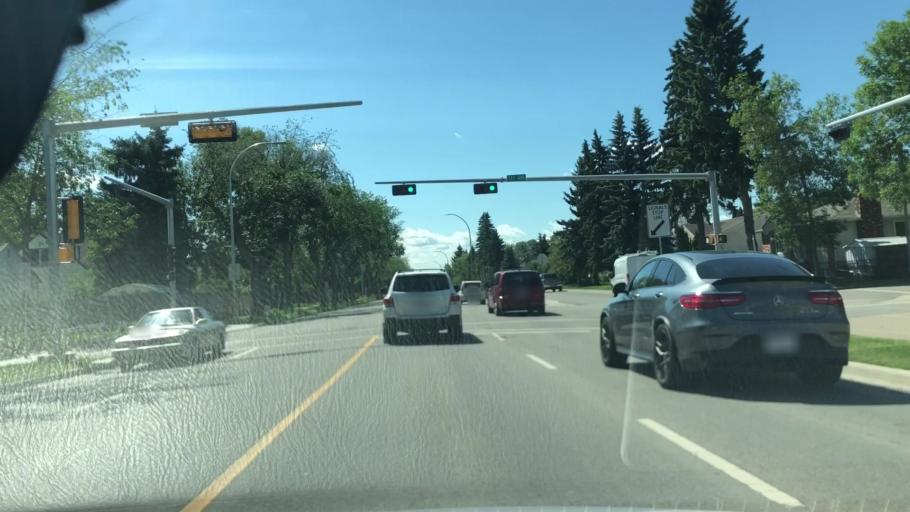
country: CA
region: Alberta
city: Edmonton
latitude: 53.5770
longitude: -113.5412
